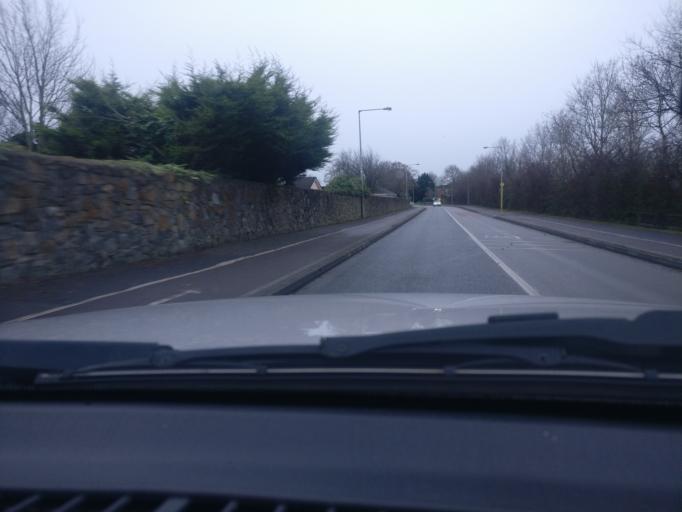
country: IE
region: Leinster
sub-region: Kildare
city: Celbridge
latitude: 53.3547
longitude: -6.5469
